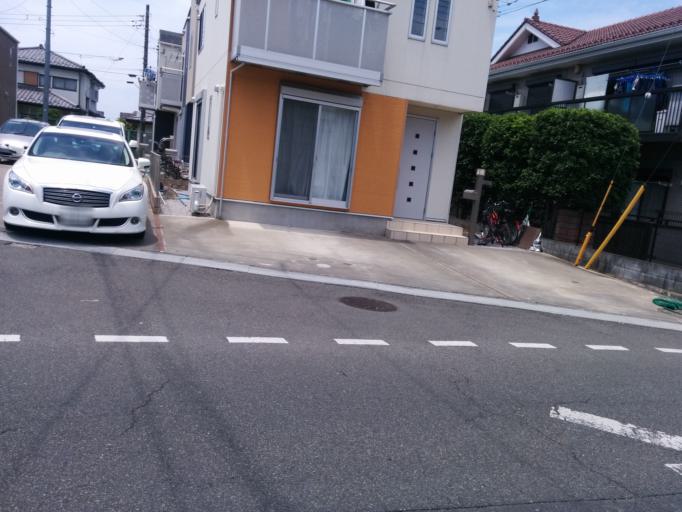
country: JP
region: Tokyo
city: Higashimurayama-shi
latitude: 35.7648
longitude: 139.4760
